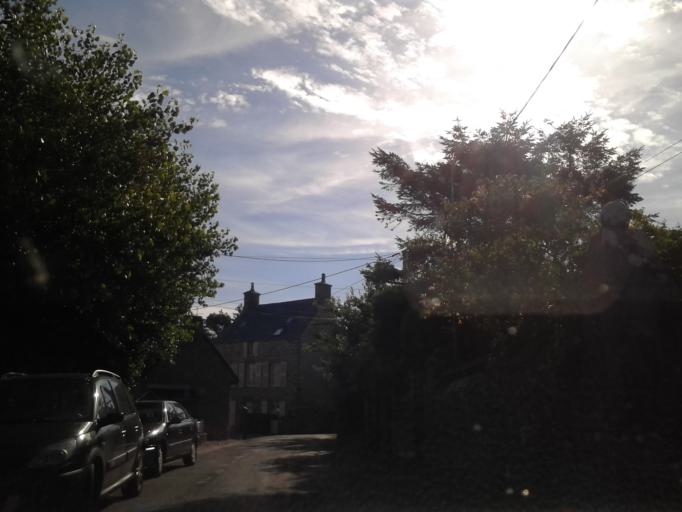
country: FR
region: Lower Normandy
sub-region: Departement de la Manche
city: Fermanville
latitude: 49.6839
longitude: -1.4678
